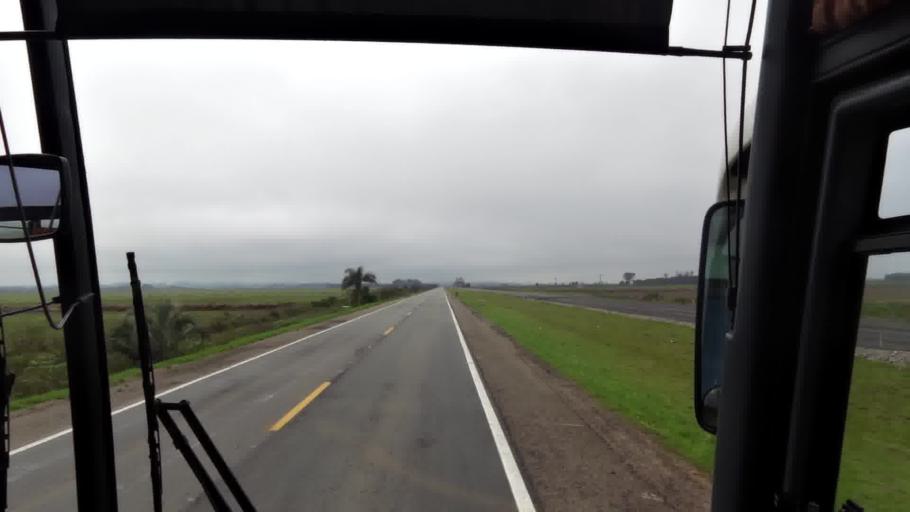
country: BR
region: Rio Grande do Sul
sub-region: Pelotas
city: Pelotas
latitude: -31.5977
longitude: -52.2894
